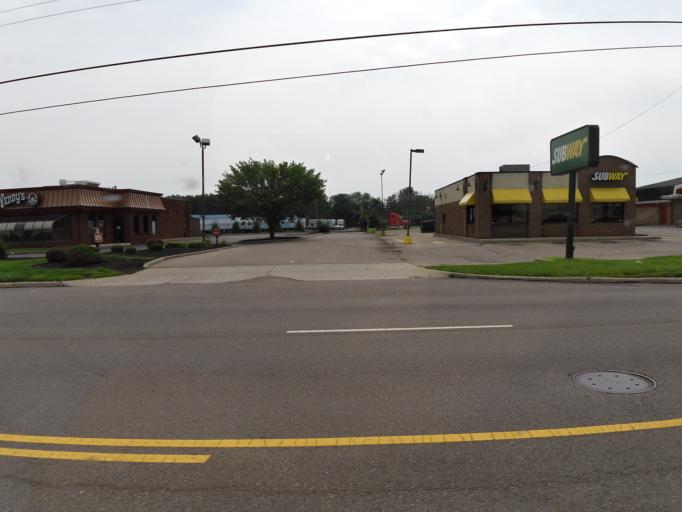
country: US
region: Ohio
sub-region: Montgomery County
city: Riverside
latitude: 39.7285
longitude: -84.1222
